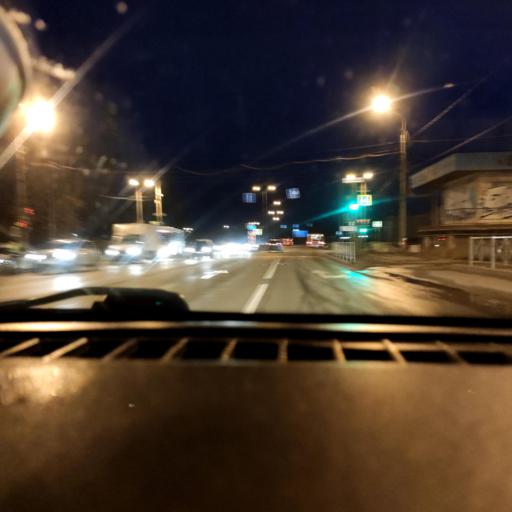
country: RU
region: Perm
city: Perm
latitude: 58.0275
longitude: 56.2180
